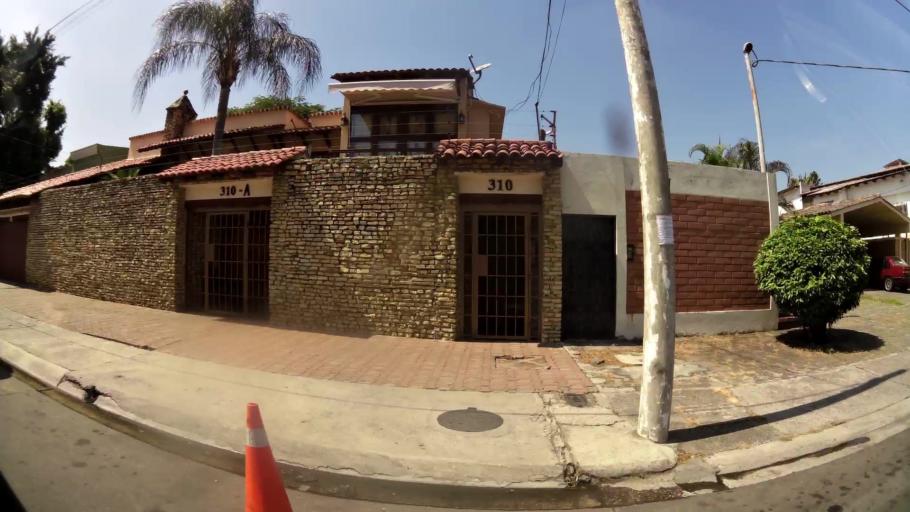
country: EC
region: Guayas
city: Guayaquil
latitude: -2.1747
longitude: -79.9095
